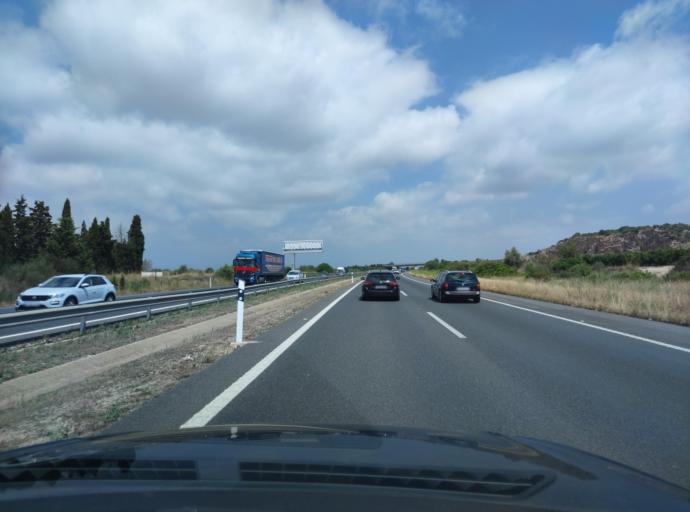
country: ES
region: Valencia
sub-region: Provincia de Castello
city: Vinaros
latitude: 40.4862
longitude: 0.4160
